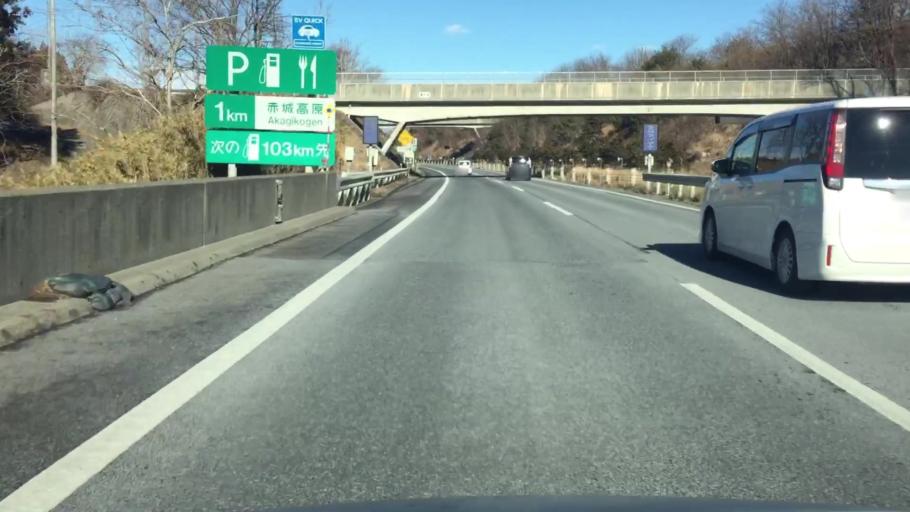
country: JP
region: Gunma
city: Numata
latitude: 36.5912
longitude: 139.0666
